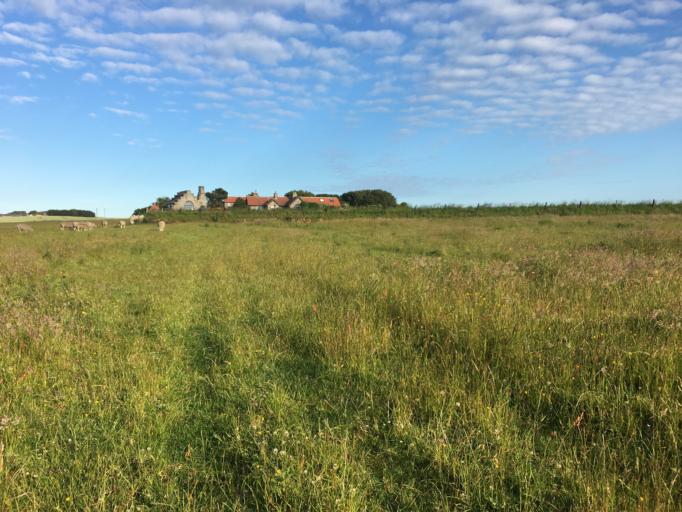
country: GB
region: England
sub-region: Northumberland
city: Bamburgh
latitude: 55.6036
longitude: -1.7030
